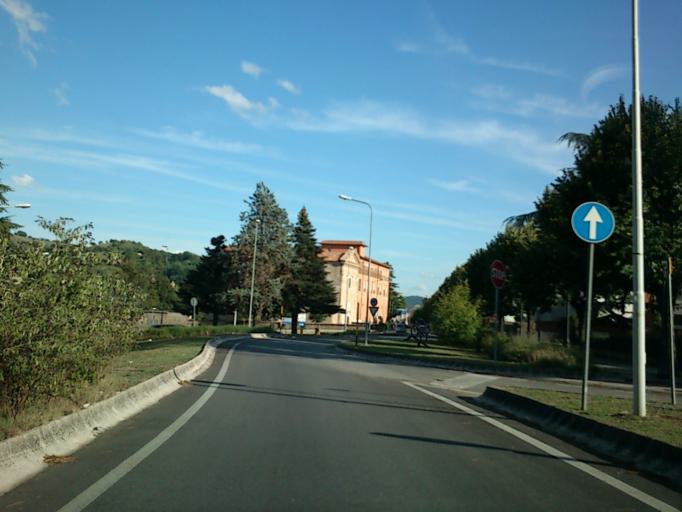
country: IT
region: The Marches
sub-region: Provincia di Pesaro e Urbino
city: Urbania
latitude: 43.6716
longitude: 12.5173
